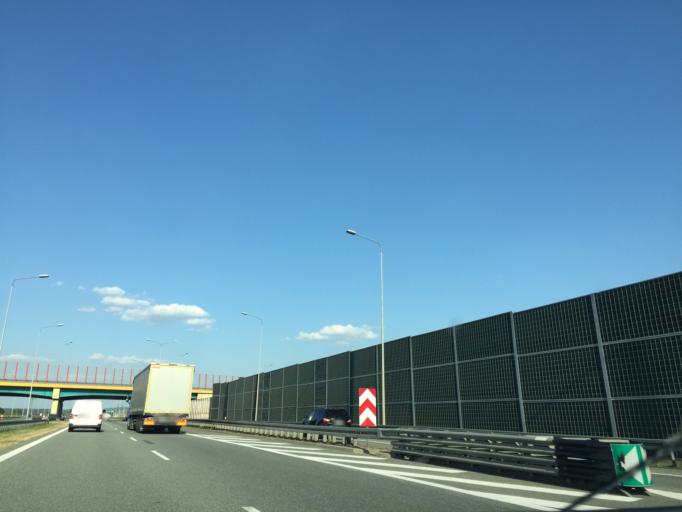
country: PL
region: Swietokrzyskie
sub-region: Powiat kielecki
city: Kostomloty Drugie
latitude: 50.9047
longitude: 20.5629
